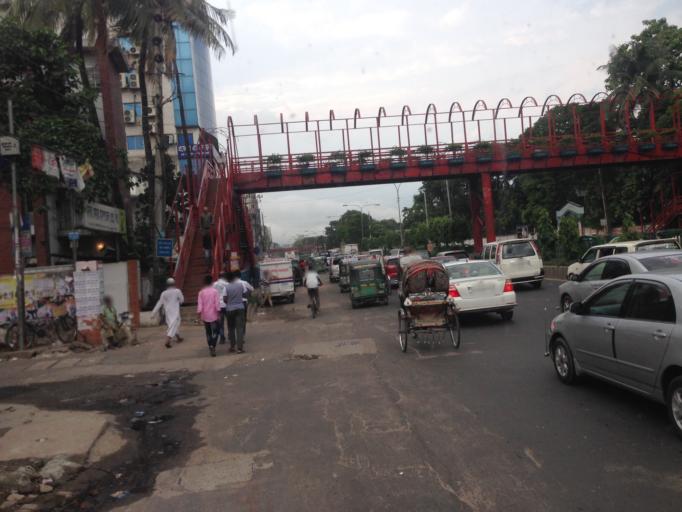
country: BD
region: Dhaka
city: Azimpur
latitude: 23.7567
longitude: 90.3749
